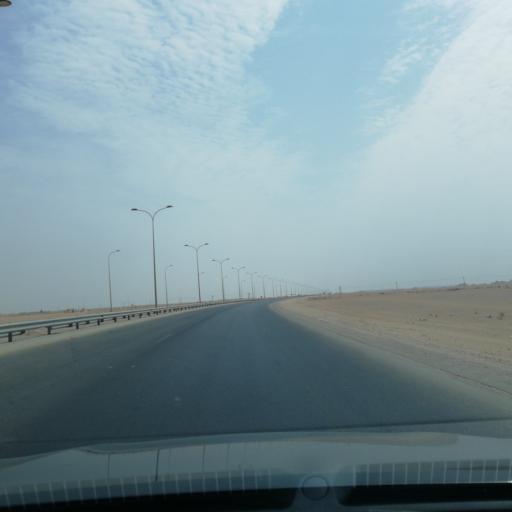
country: OM
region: Zufar
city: Salalah
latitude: 17.6342
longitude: 54.0327
